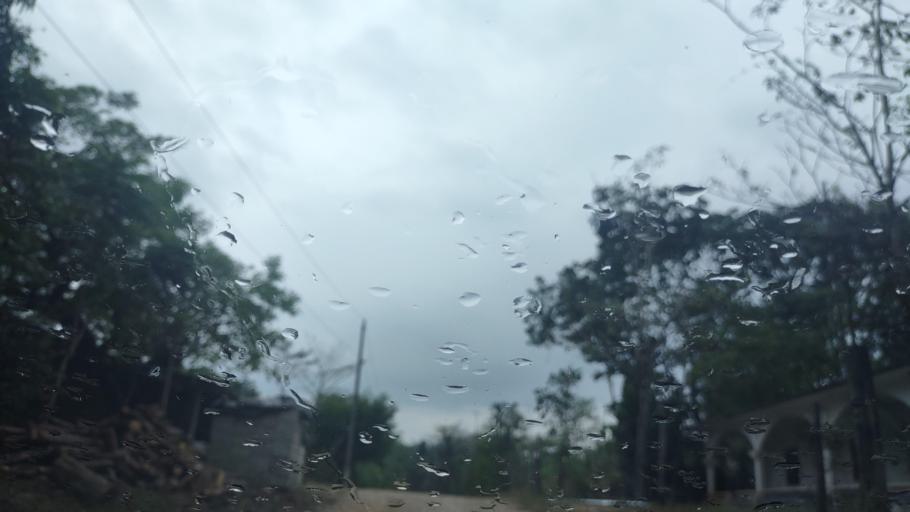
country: MX
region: Veracruz
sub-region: Uxpanapa
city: Poblado 10
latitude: 17.4499
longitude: -94.0965
